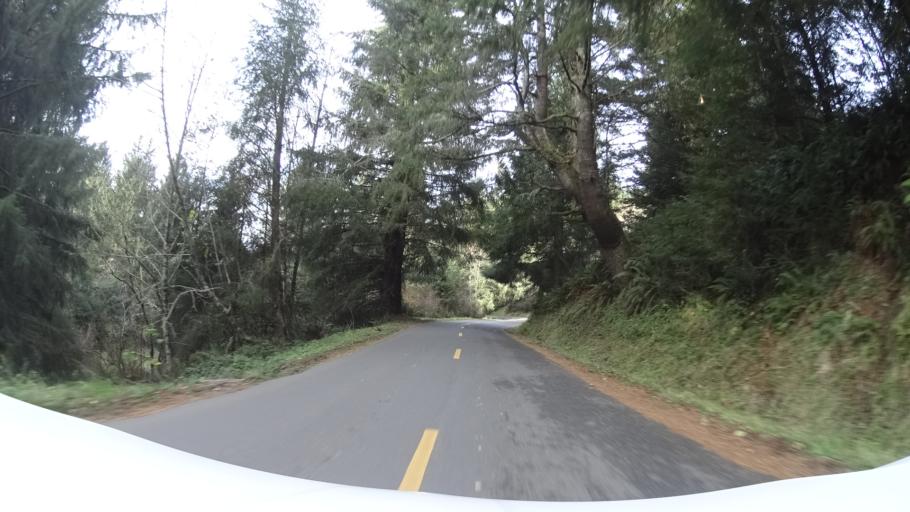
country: US
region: California
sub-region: Humboldt County
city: Ferndale
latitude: 40.5445
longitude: -124.2746
